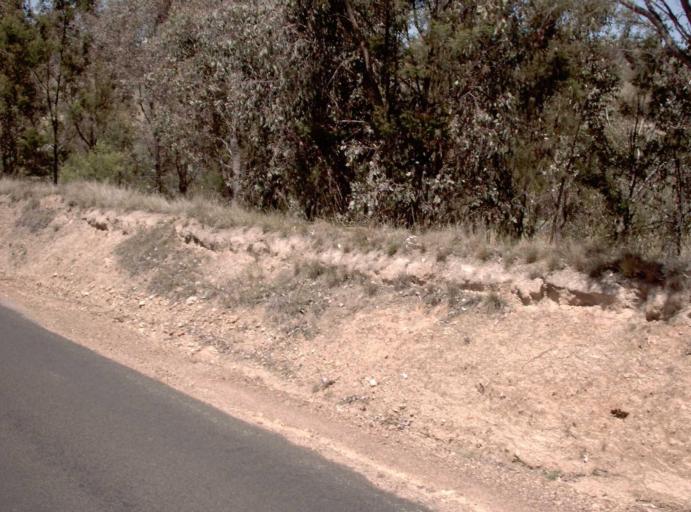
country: AU
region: Victoria
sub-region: East Gippsland
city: Bairnsdale
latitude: -37.1698
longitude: 147.6902
